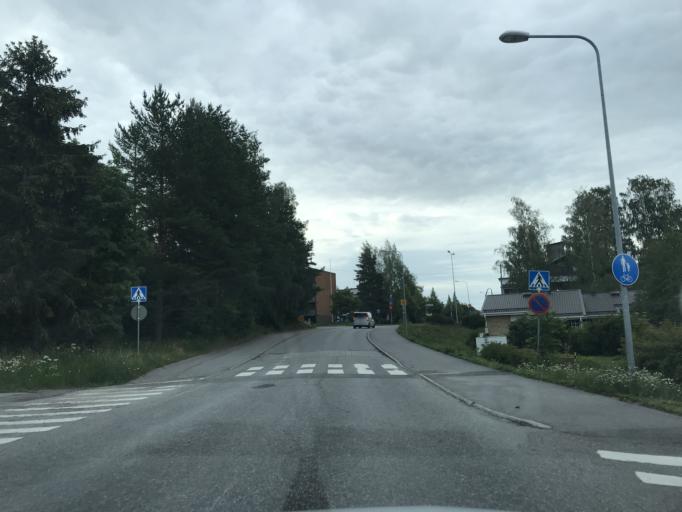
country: FI
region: Uusimaa
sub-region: Helsinki
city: Nurmijaervi
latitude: 60.3780
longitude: 24.7499
